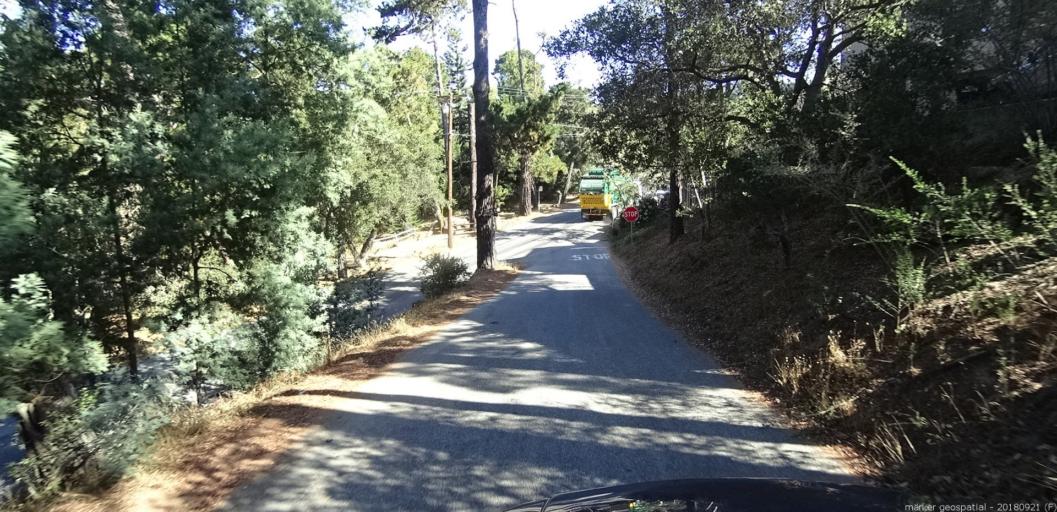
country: US
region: California
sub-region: Monterey County
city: Carmel-by-the-Sea
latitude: 36.5627
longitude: -121.9191
